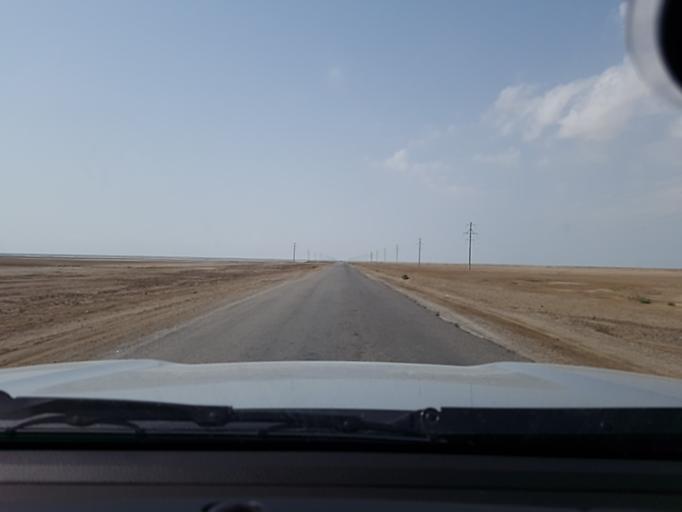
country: TM
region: Balkan
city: Gumdag
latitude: 39.0905
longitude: 54.5845
